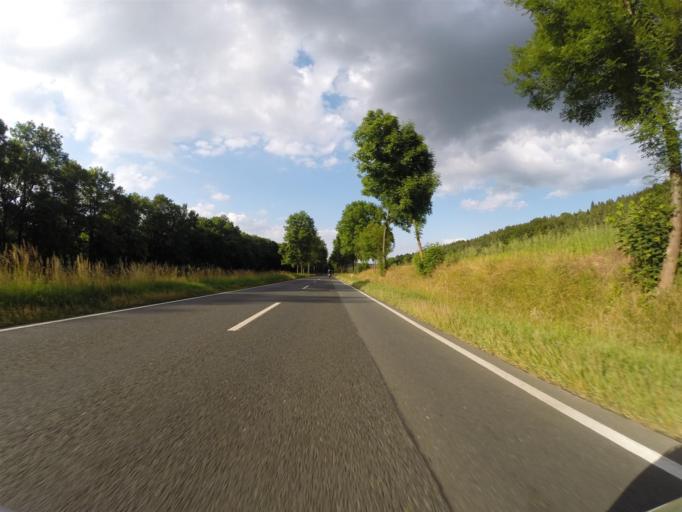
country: DE
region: Thuringia
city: Barchfeld
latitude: 50.8388
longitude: 11.1870
